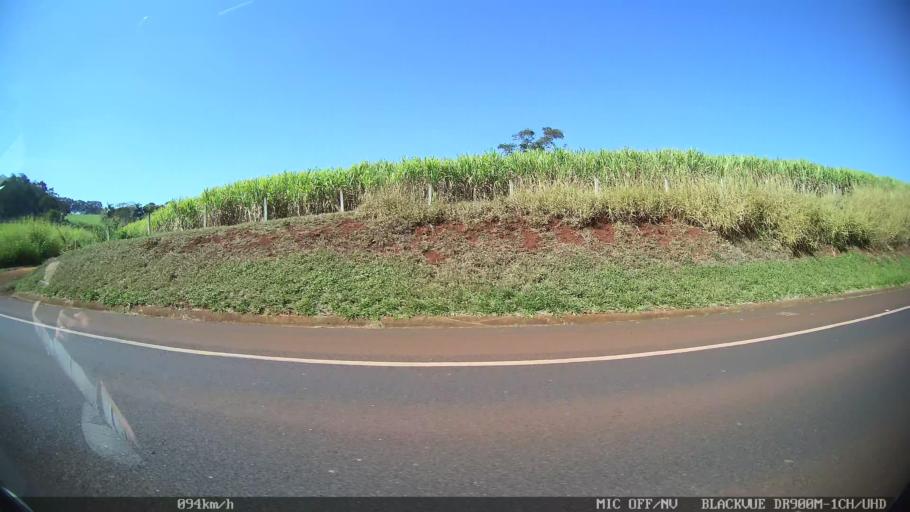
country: BR
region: Sao Paulo
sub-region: Franca
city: Franca
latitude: -20.6296
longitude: -47.4653
